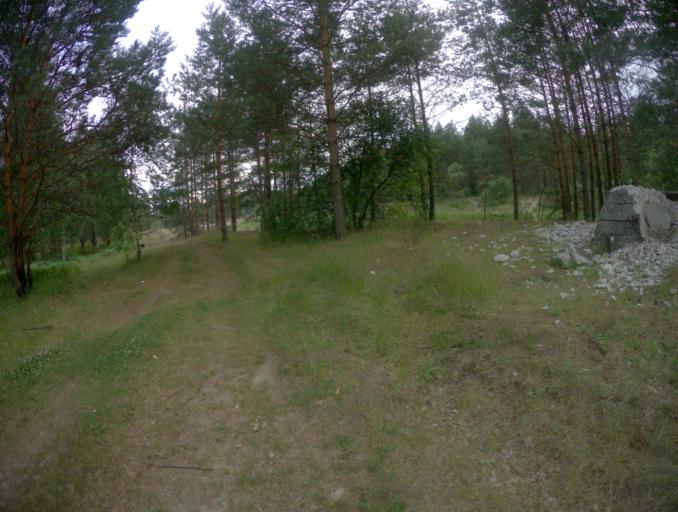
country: RU
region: Nizjnij Novgorod
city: Frolishchi
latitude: 56.4522
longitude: 42.6811
